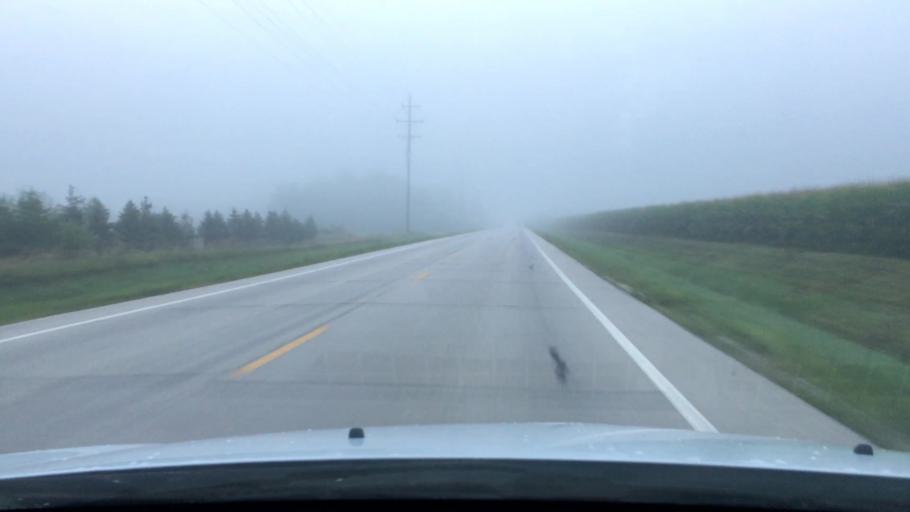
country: US
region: Illinois
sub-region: DeKalb County
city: Waterman
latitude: 41.8491
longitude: -88.7923
